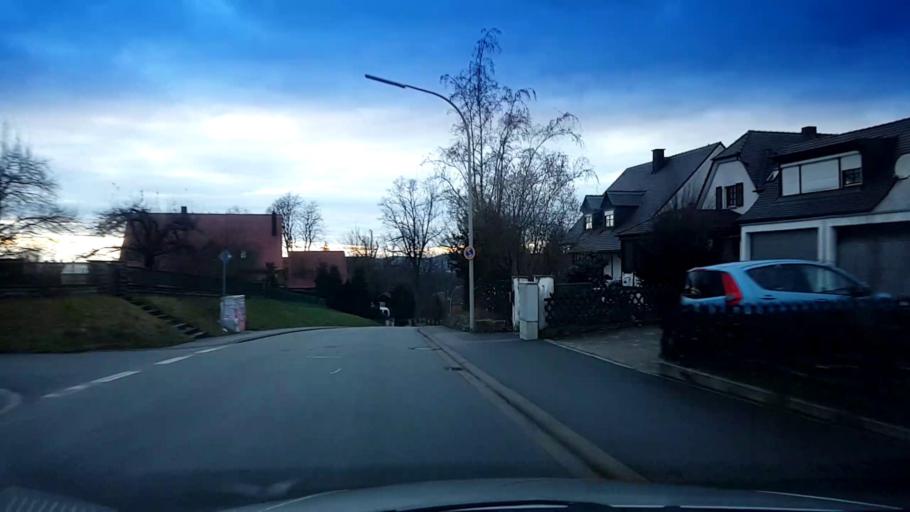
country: DE
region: Bavaria
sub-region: Upper Franconia
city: Memmelsdorf
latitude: 49.9320
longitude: 10.9604
